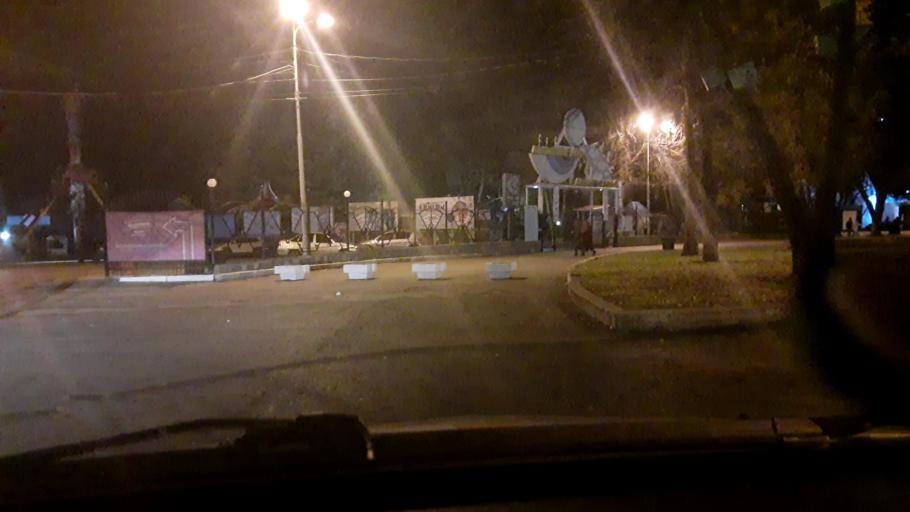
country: RU
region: Bashkortostan
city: Ufa
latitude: 54.7731
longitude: 56.0225
